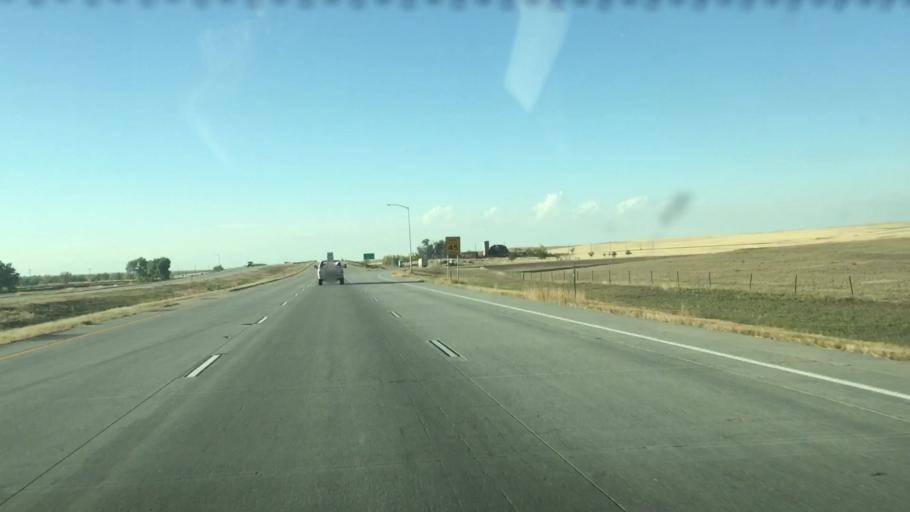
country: US
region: Colorado
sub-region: Arapahoe County
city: Byers
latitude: 39.5019
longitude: -103.9689
